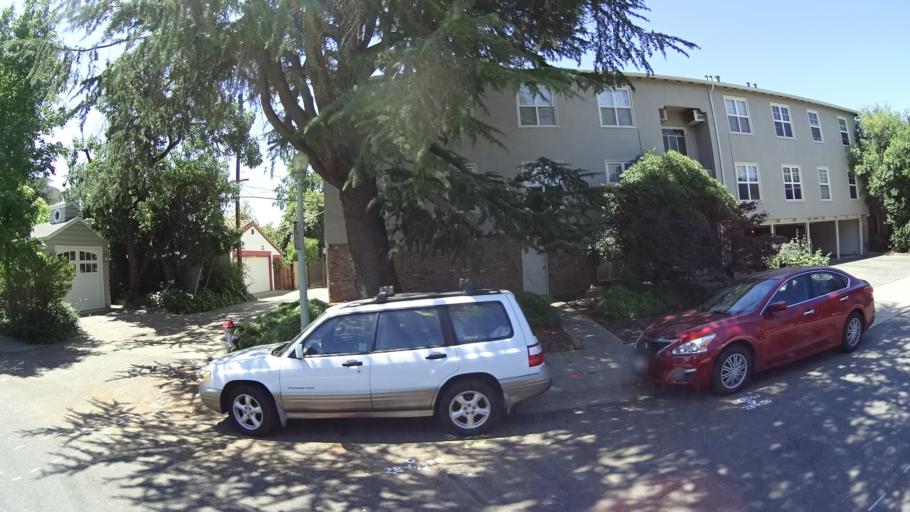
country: US
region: California
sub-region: Sacramento County
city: Sacramento
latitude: 38.5439
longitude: -121.4891
